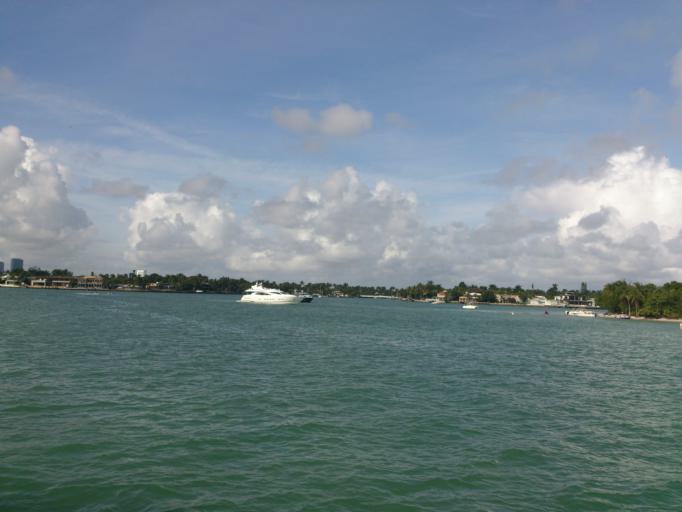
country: US
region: Florida
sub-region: Miami-Dade County
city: Miami Beach
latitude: 25.7828
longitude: -80.1531
